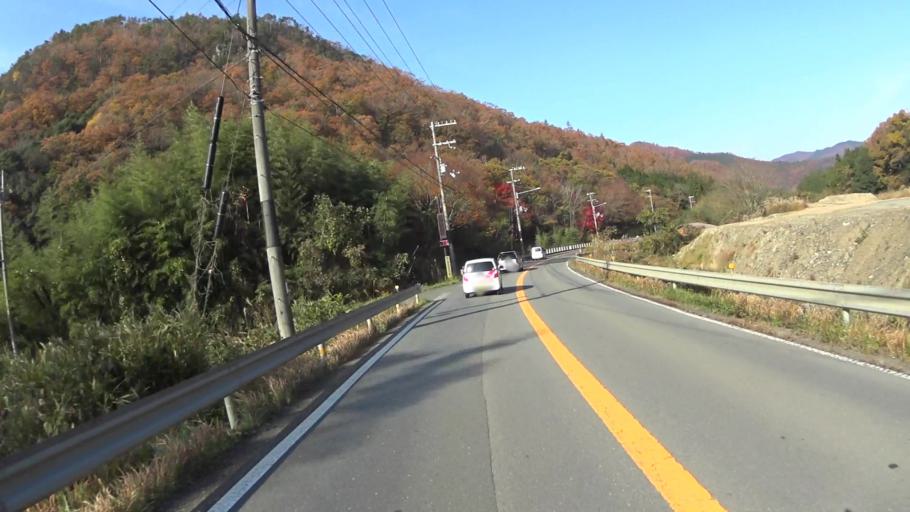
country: JP
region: Kyoto
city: Ayabe
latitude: 35.1929
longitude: 135.2883
